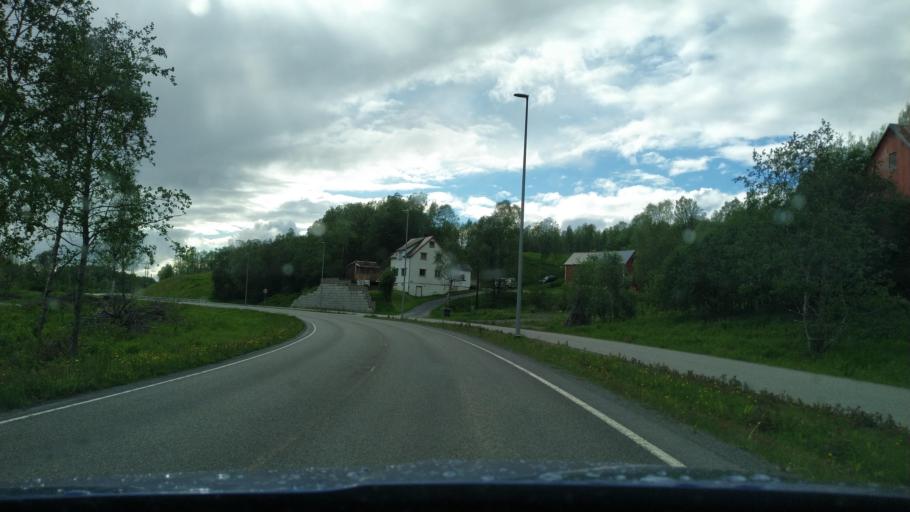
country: NO
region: Troms
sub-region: Sorreisa
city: Sorreisa
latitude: 69.1745
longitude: 18.1018
